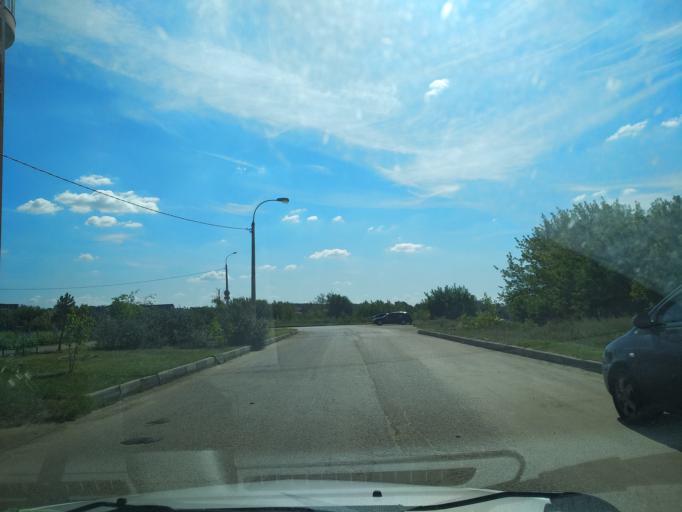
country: RU
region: Moskovskaya
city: Bykovo
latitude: 55.5923
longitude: 38.0900
